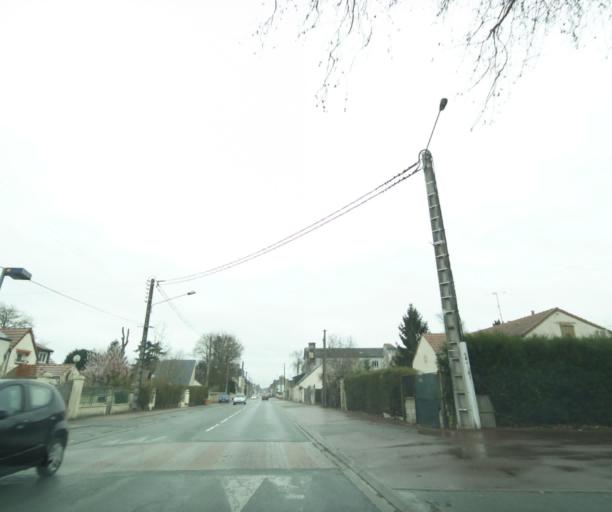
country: FR
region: Centre
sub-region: Departement du Loiret
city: Chevilly
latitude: 48.0321
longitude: 1.8743
